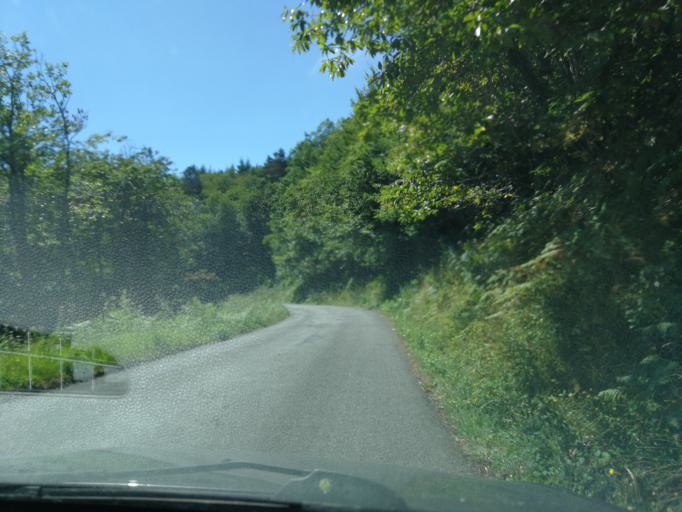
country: FR
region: Limousin
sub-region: Departement de la Correze
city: Argentat
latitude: 45.0978
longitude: 1.8912
